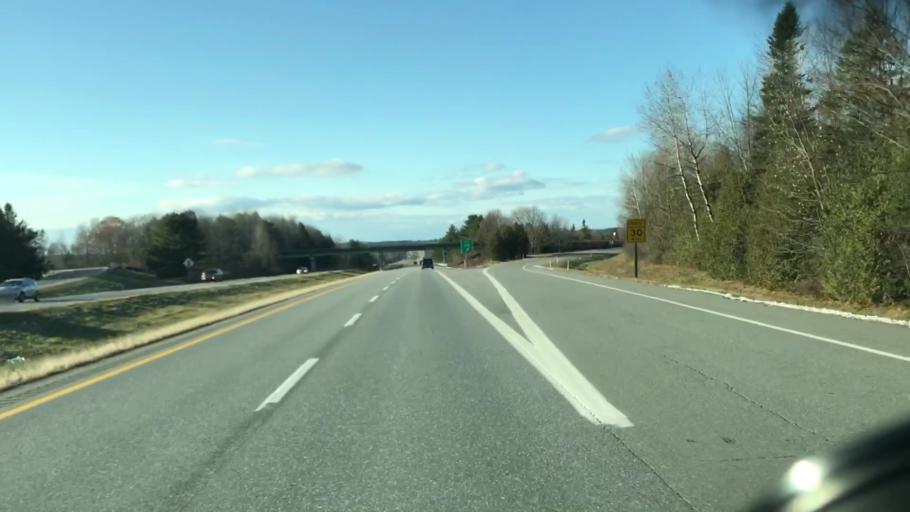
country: US
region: Maine
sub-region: Penobscot County
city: Newport
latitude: 44.8174
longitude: -69.2565
